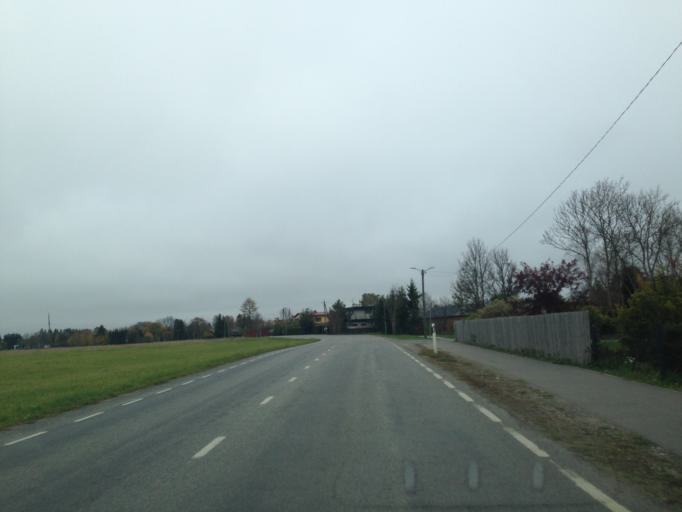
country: EE
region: Harju
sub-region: Saue linn
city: Saue
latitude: 59.3297
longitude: 24.5475
